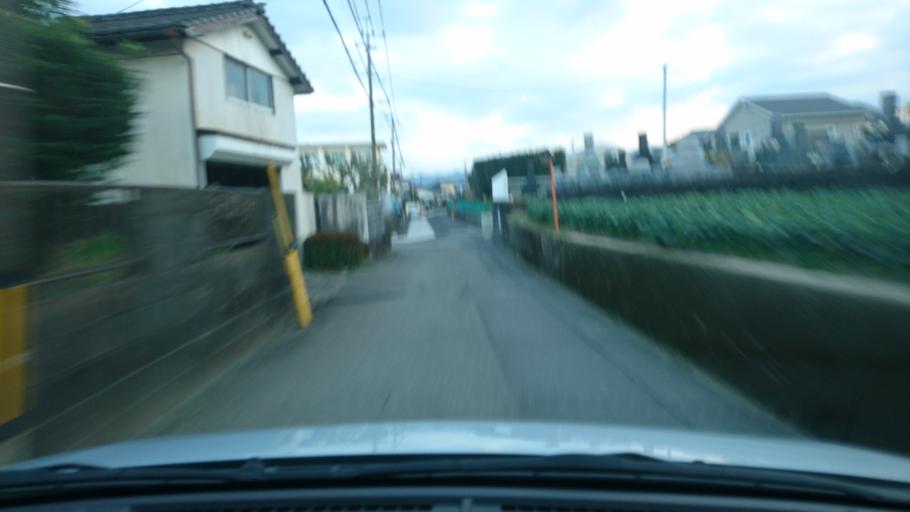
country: JP
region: Miyazaki
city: Miyazaki-shi
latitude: 31.8601
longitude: 131.4309
